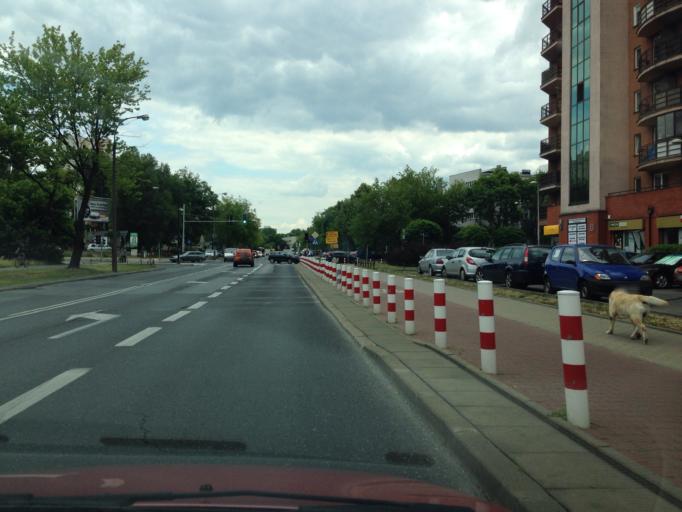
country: PL
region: Masovian Voivodeship
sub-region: Warszawa
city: Bielany
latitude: 52.2674
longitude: 20.9470
